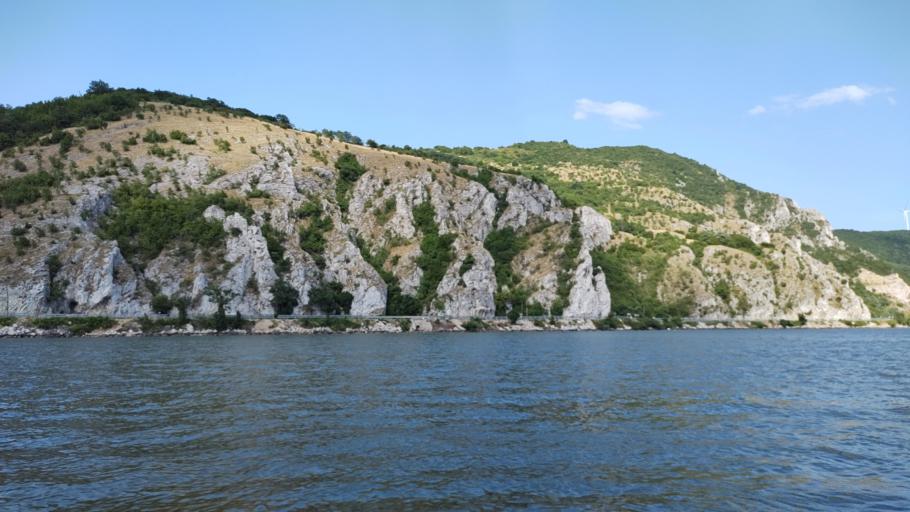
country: RO
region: Caras-Severin
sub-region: Comuna Pescari
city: Coronini
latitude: 44.6656
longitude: 21.6913
